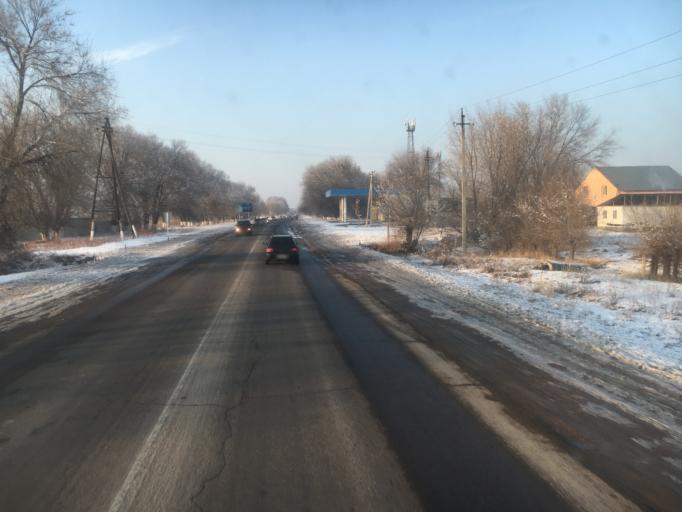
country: KZ
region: Almaty Oblysy
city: Burunday
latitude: 43.3343
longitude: 76.6608
